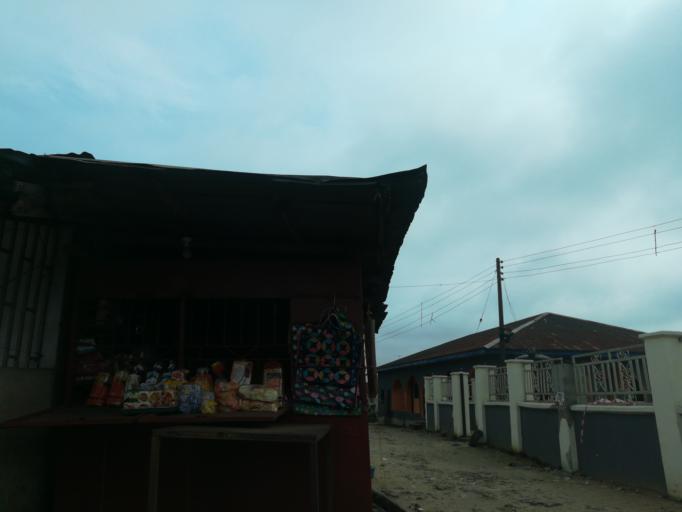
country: NG
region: Rivers
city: Port Harcourt
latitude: 4.8746
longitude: 6.9881
